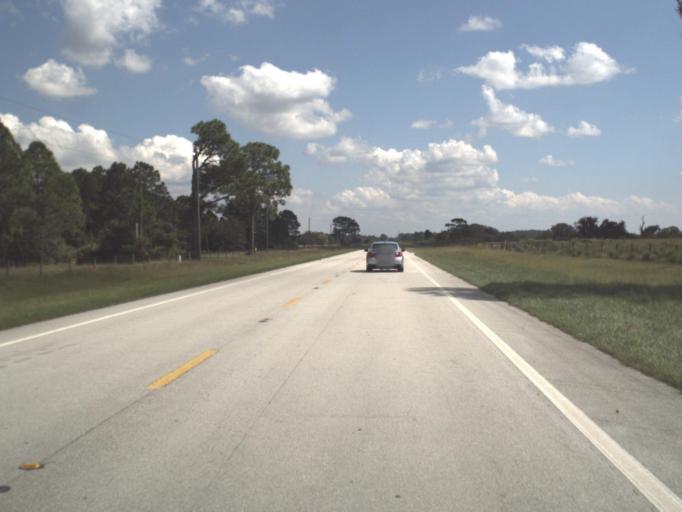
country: US
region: Florida
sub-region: Okeechobee County
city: Okeechobee
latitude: 27.3723
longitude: -81.0845
